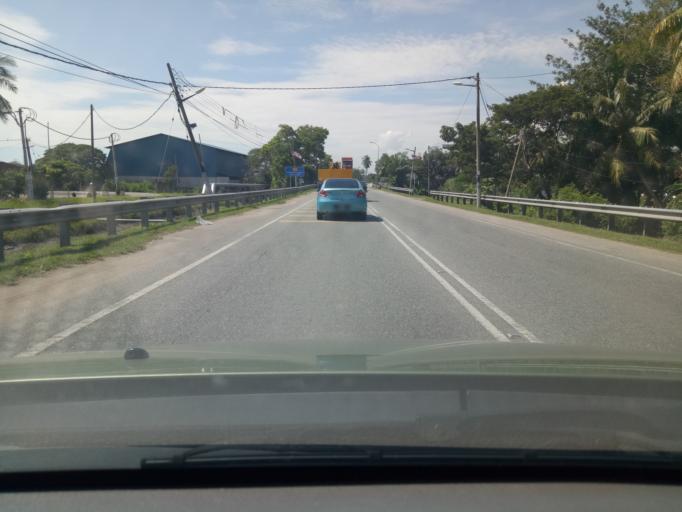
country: MY
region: Kedah
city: Alor Setar
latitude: 5.9691
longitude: 100.4018
